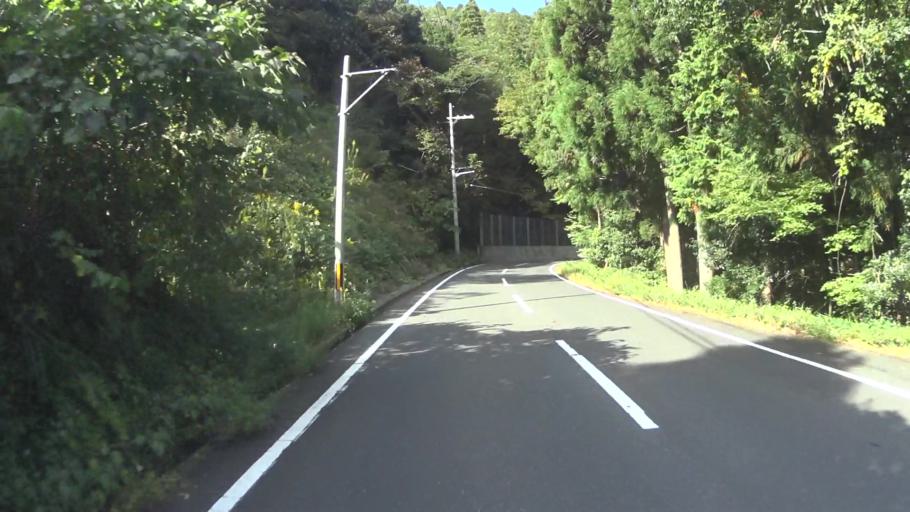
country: JP
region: Kyoto
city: Maizuru
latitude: 35.5316
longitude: 135.4410
